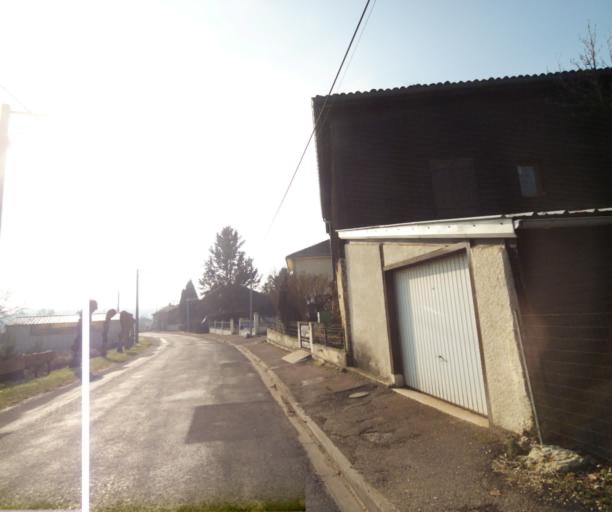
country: FR
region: Champagne-Ardenne
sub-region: Departement de la Haute-Marne
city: Laneuville-a-Remy
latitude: 48.4613
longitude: 4.9149
